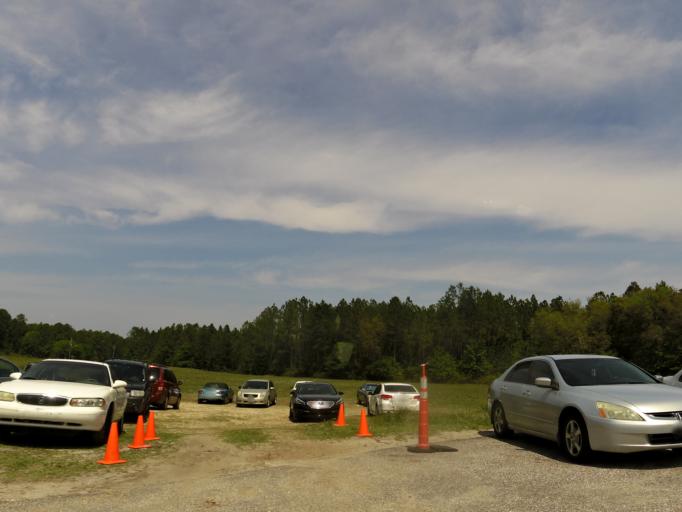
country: US
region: Florida
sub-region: Nassau County
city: Nassau Village-Ratliff
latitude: 30.4977
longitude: -81.6656
